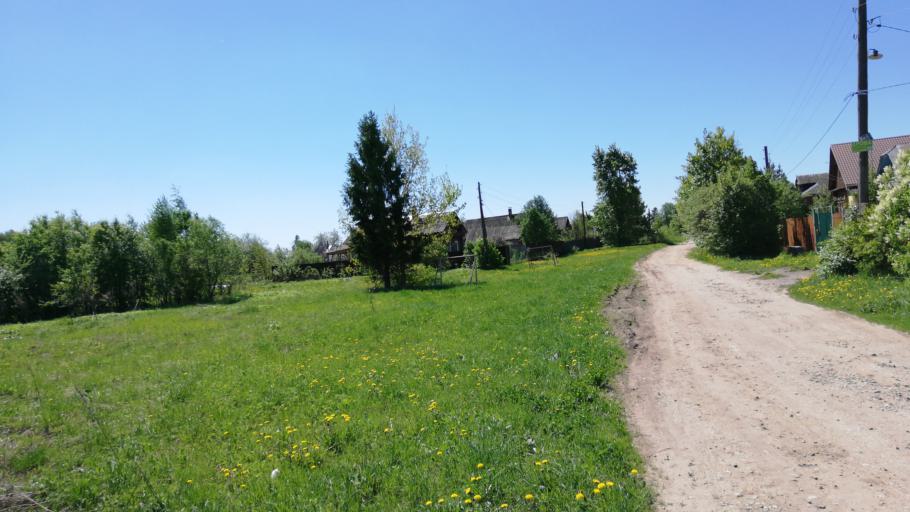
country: RU
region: Ivanovo
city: Pistsovo
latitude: 57.1183
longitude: 40.5975
